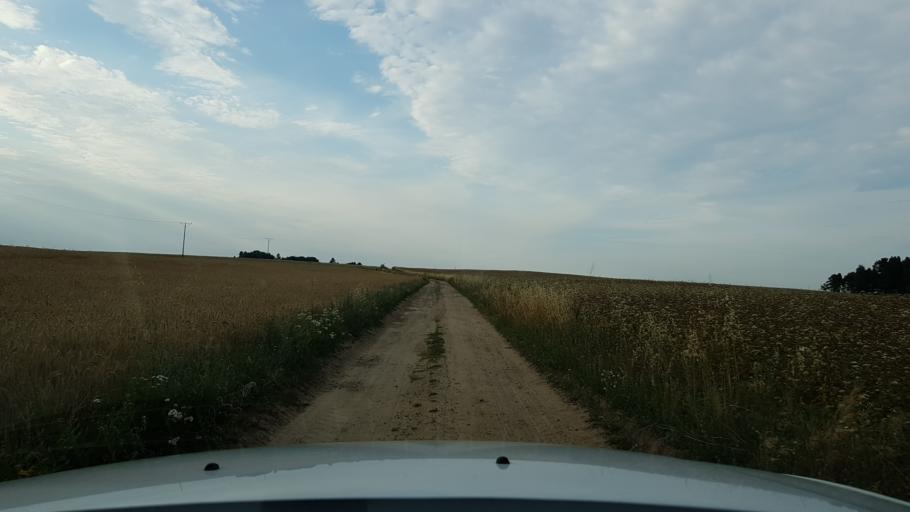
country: PL
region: West Pomeranian Voivodeship
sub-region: Powiat swidwinski
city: Polczyn-Zdroj
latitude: 53.7937
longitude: 16.0814
